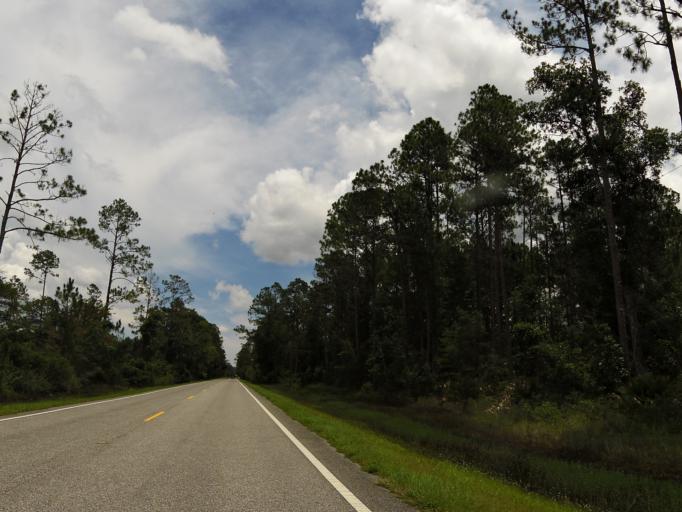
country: US
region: Florida
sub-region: Flagler County
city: Palm Coast
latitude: 29.6540
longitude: -81.3543
